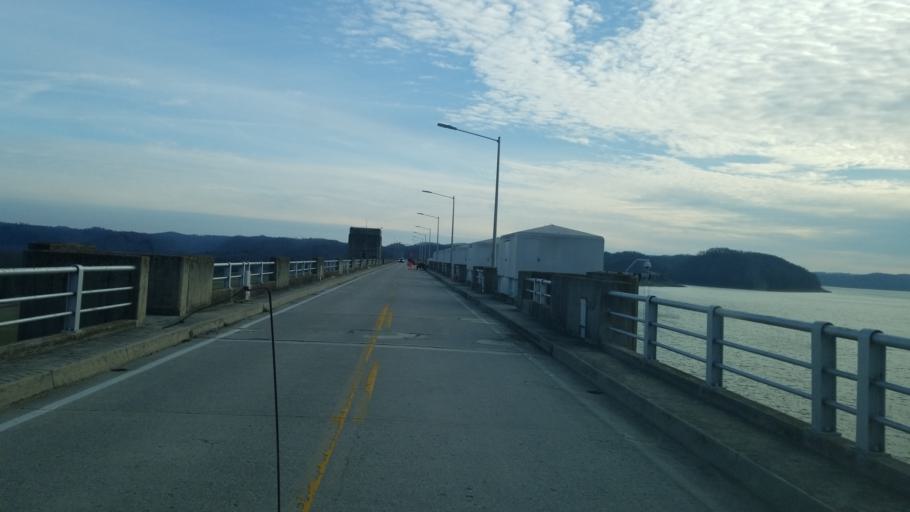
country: US
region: Kentucky
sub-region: Russell County
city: Jamestown
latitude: 36.8682
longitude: -85.1482
